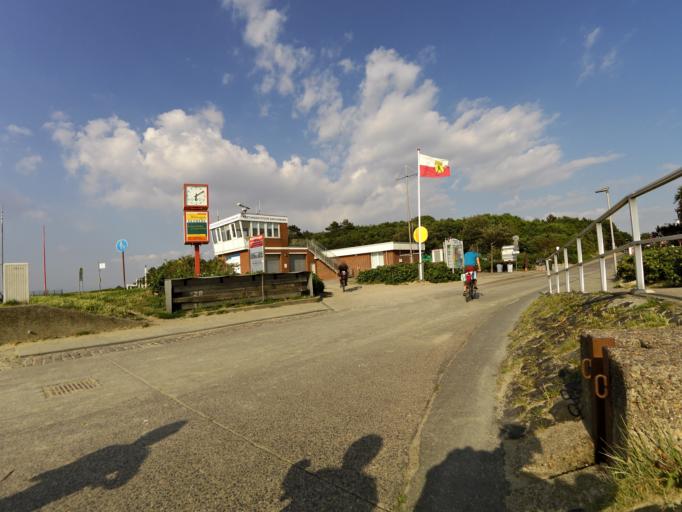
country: DE
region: Lower Saxony
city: Nordholz
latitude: 53.8631
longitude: 8.5958
